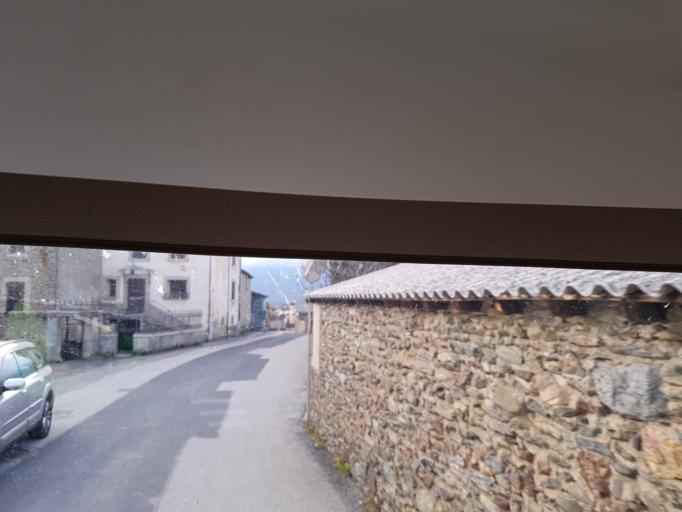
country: FR
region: Languedoc-Roussillon
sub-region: Departement des Pyrenees-Orientales
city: Osseja
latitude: 42.4401
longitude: 2.0299
